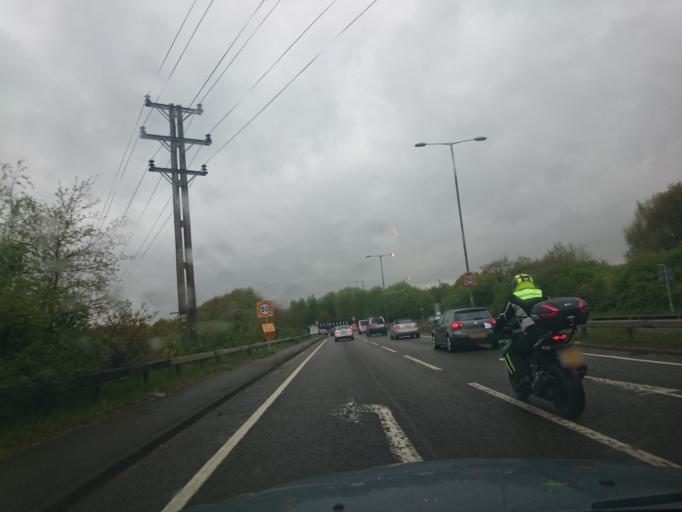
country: GB
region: England
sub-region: Surrey
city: Hale
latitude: 51.2201
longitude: -0.7742
